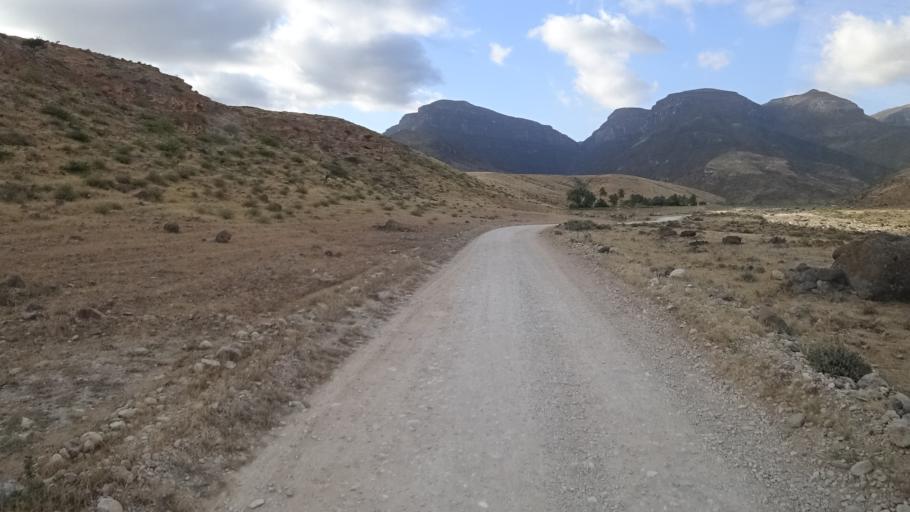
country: OM
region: Zufar
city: Salalah
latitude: 16.9863
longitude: 53.8476
